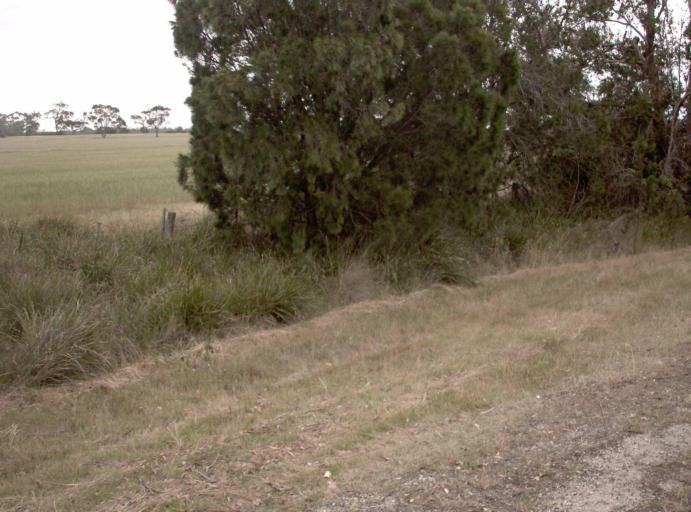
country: AU
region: Victoria
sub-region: Wellington
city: Sale
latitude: -38.1319
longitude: 147.4217
